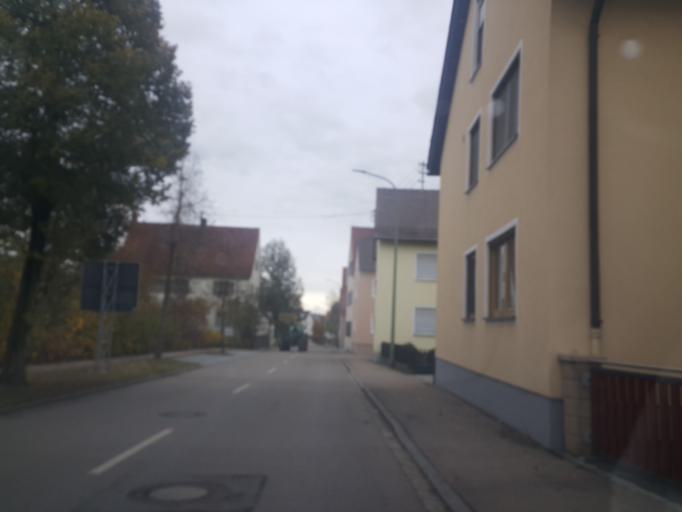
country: DE
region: Bavaria
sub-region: Swabia
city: Marxheim
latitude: 48.7417
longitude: 10.9475
